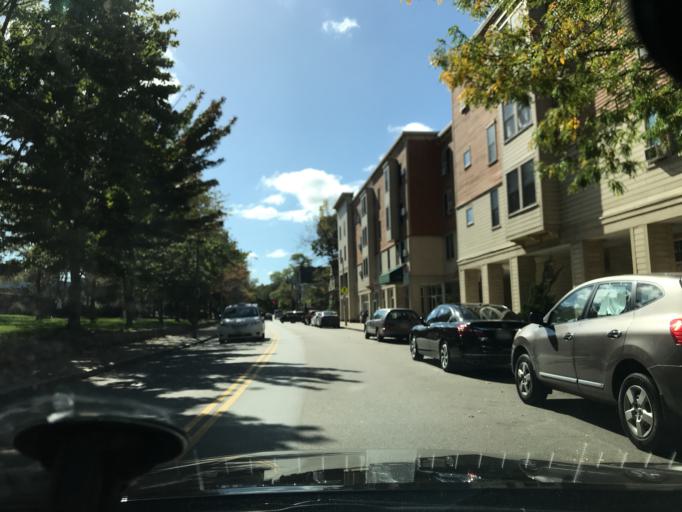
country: US
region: Massachusetts
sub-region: Suffolk County
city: Jamaica Plain
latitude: 42.3186
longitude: -71.1038
